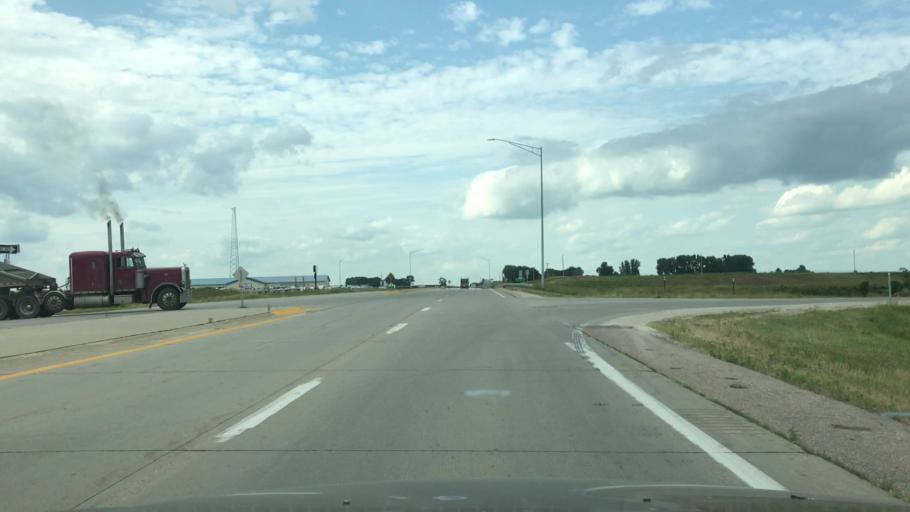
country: US
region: Iowa
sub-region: Plymouth County
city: Le Mars
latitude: 42.8164
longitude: -96.1746
